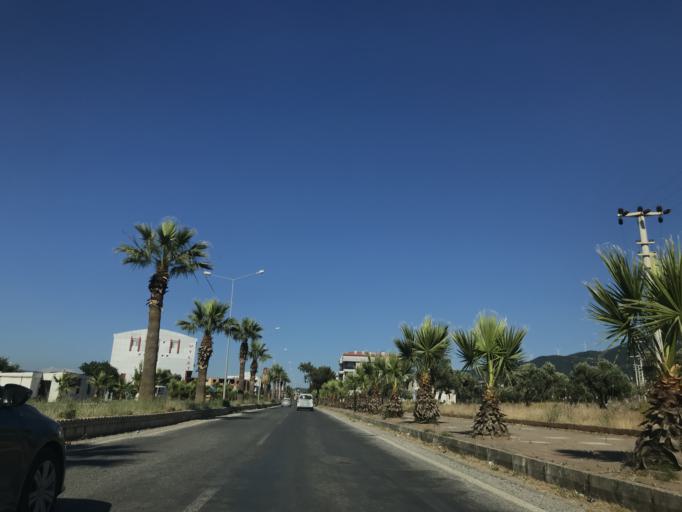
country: TR
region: Aydin
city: Davutlar
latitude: 37.7329
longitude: 27.2759
